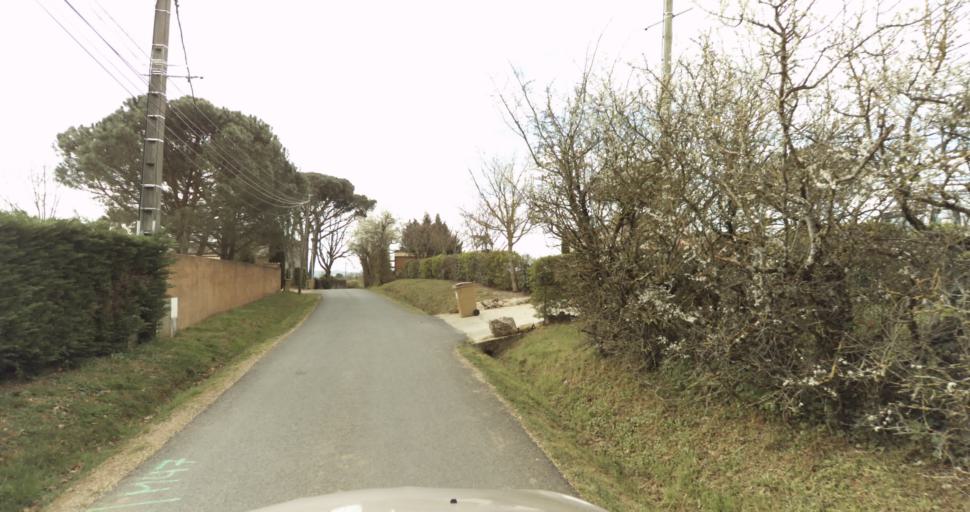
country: FR
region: Midi-Pyrenees
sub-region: Departement du Tarn
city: Puygouzon
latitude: 43.8696
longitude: 2.1915
